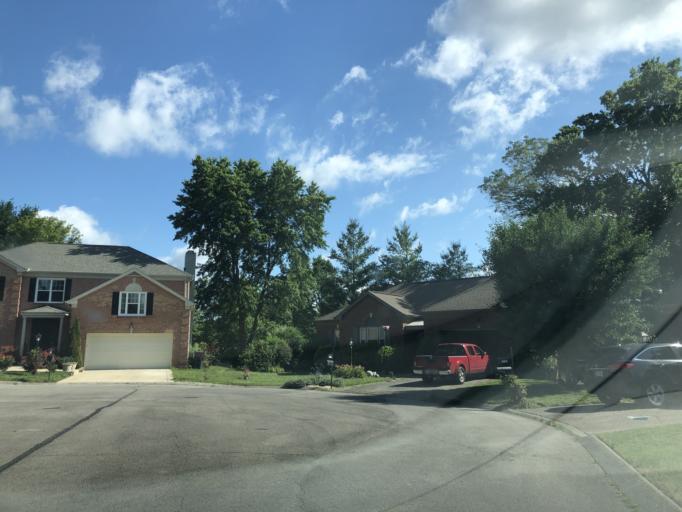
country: US
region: Tennessee
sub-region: Davidson County
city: Belle Meade
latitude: 36.0615
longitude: -86.9536
